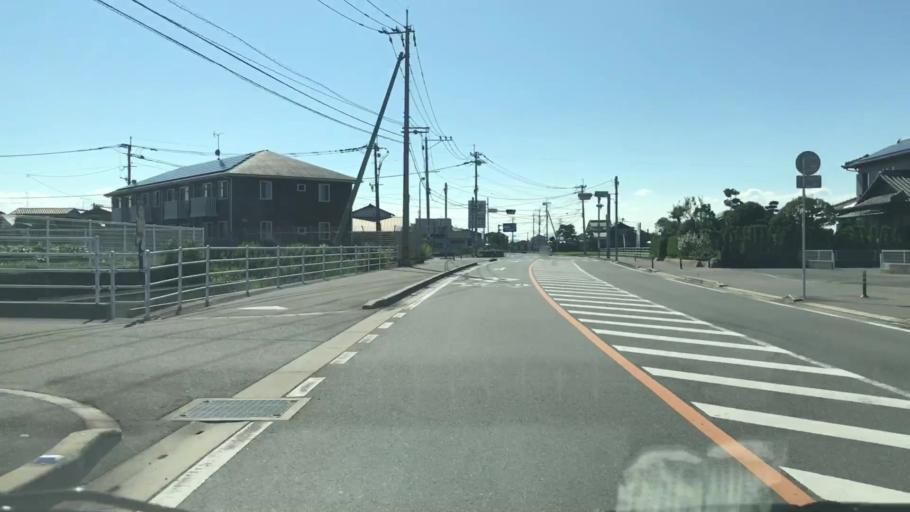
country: JP
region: Saga Prefecture
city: Okawa
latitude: 33.2300
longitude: 130.3595
